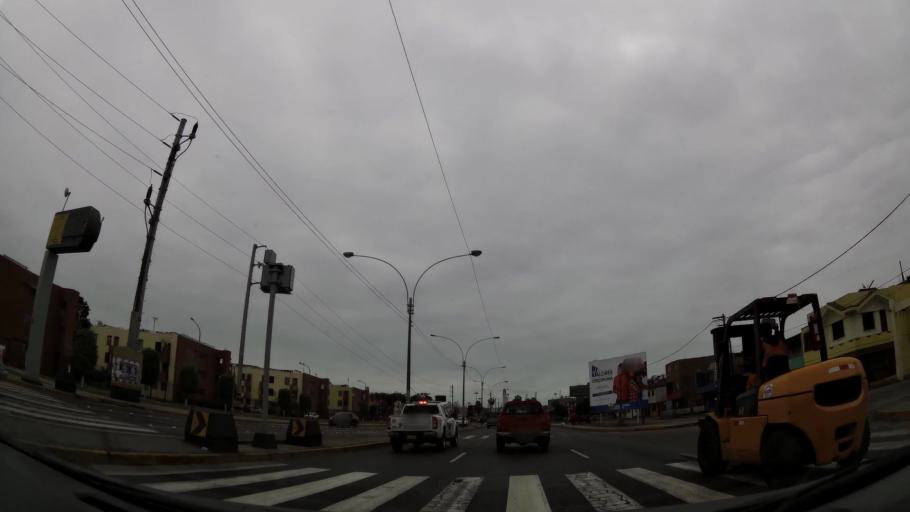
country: PE
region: Callao
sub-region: Callao
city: Callao
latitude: -12.0513
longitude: -77.1316
